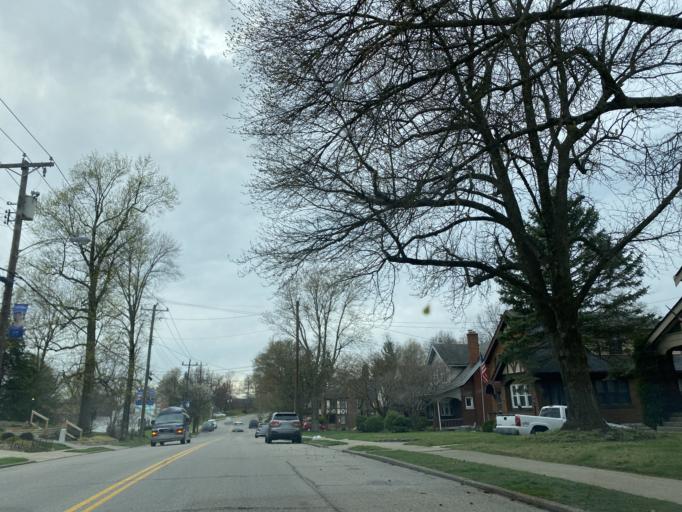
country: US
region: Kentucky
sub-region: Campbell County
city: Fort Thomas
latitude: 39.0757
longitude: -84.4558
